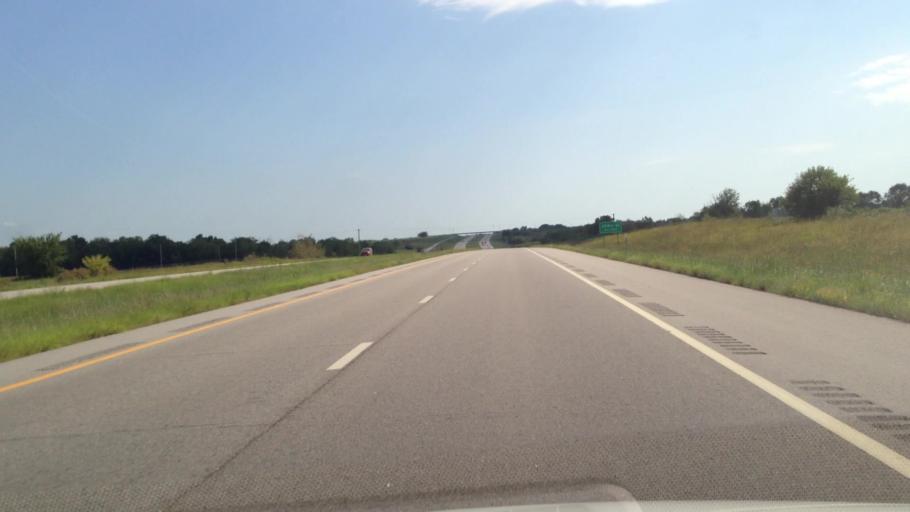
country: US
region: Kansas
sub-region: Linn County
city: La Cygne
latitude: 38.4213
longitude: -94.6877
